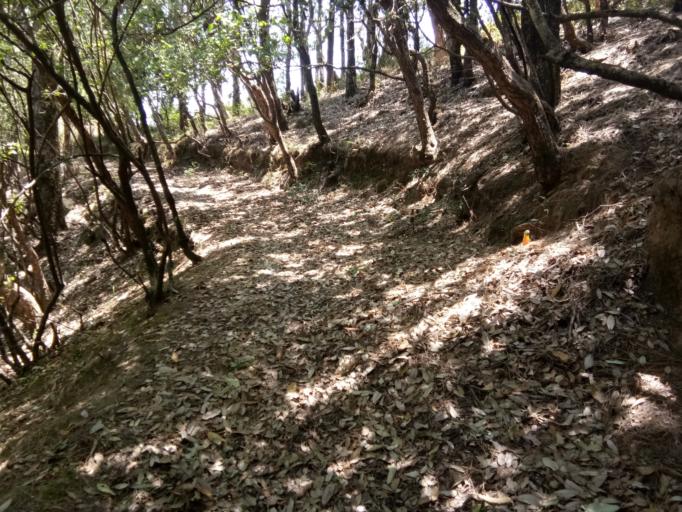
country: IN
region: Uttarakhand
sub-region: Naini Tal
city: Bhim Tal
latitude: 29.3689
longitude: 79.6069
